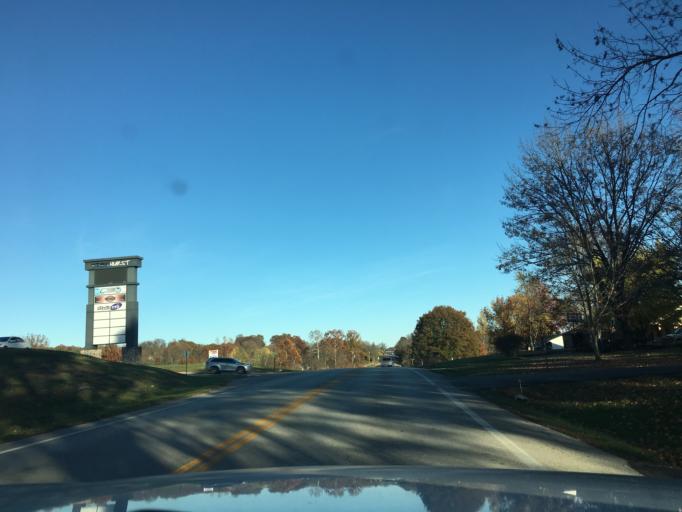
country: US
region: Missouri
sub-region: Franklin County
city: New Haven
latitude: 38.6004
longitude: -91.2354
